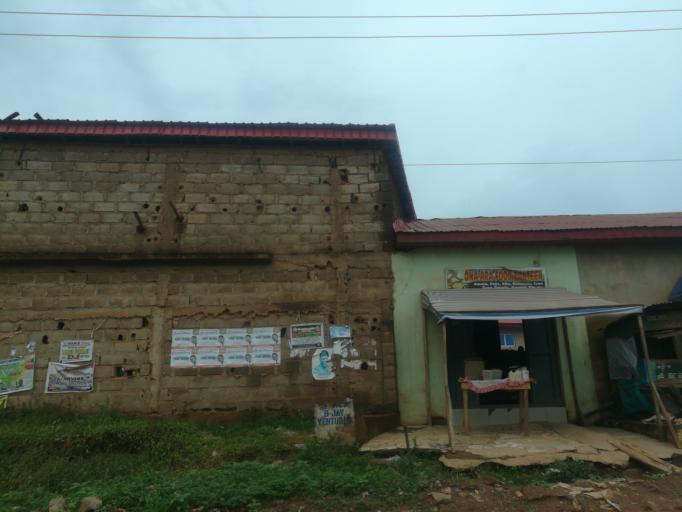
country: NG
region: Oyo
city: Ibadan
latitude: 7.3914
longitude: 3.9599
